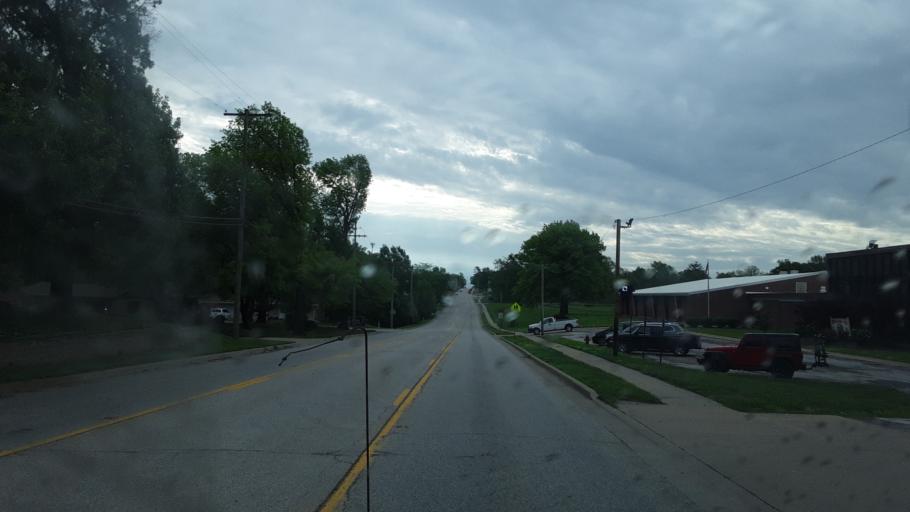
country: US
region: Illinois
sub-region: Hancock County
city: Hamilton
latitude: 40.3965
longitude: -91.3448
